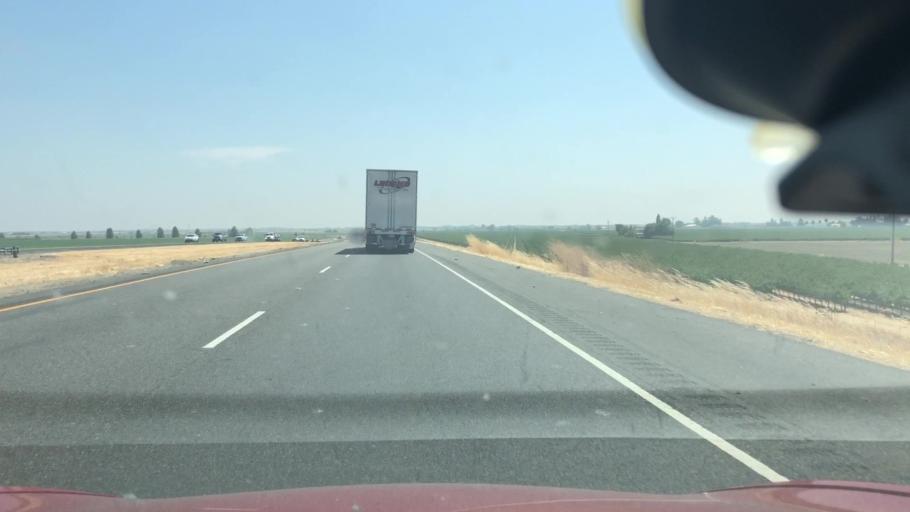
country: US
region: California
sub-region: Sacramento County
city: Walnut Grove
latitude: 38.3200
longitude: -121.4655
